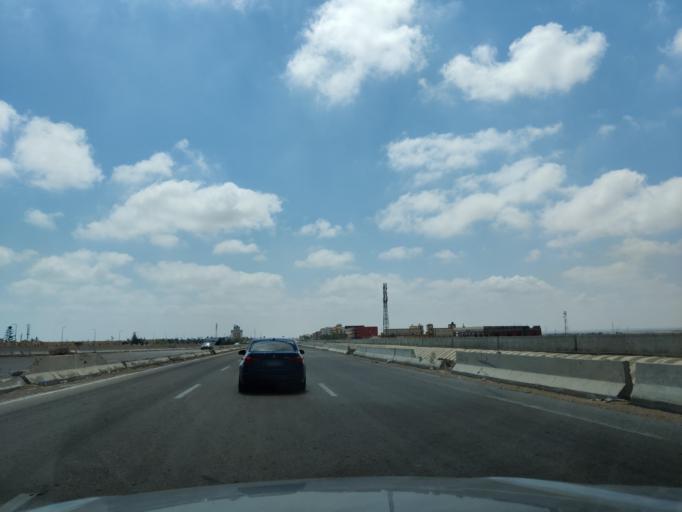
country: EG
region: Muhafazat Matruh
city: Al `Alamayn
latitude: 30.8206
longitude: 29.0172
